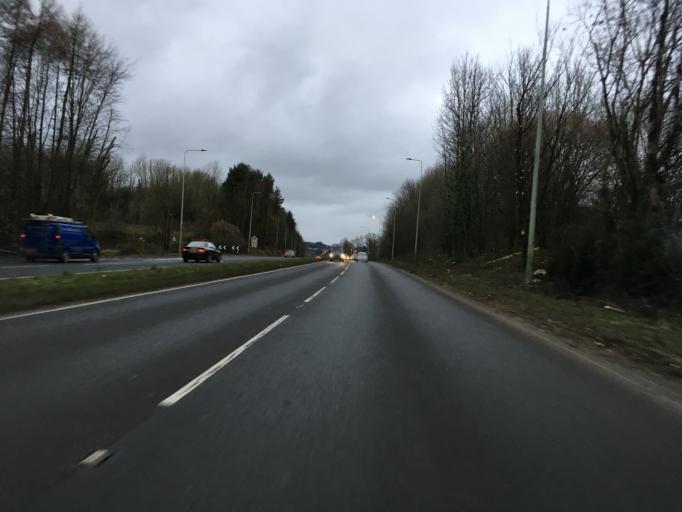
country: GB
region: Wales
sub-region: Rhondda Cynon Taf
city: Llantrisant
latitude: 51.5190
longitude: -3.3594
